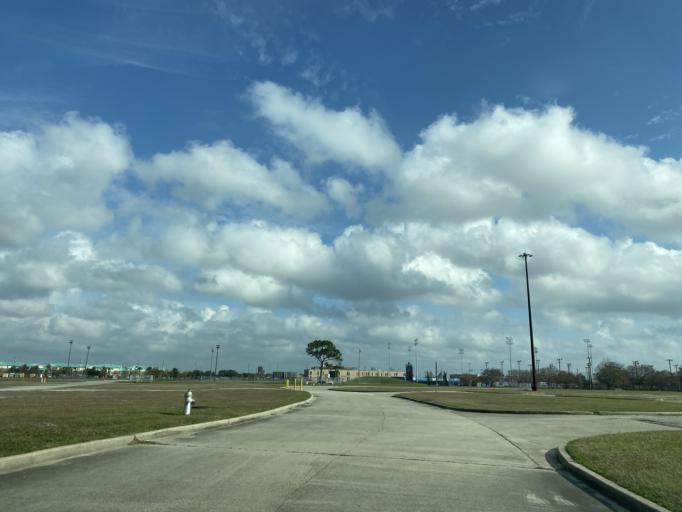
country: US
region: Louisiana
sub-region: Orleans Parish
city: New Orleans
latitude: 30.0322
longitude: -90.0510
